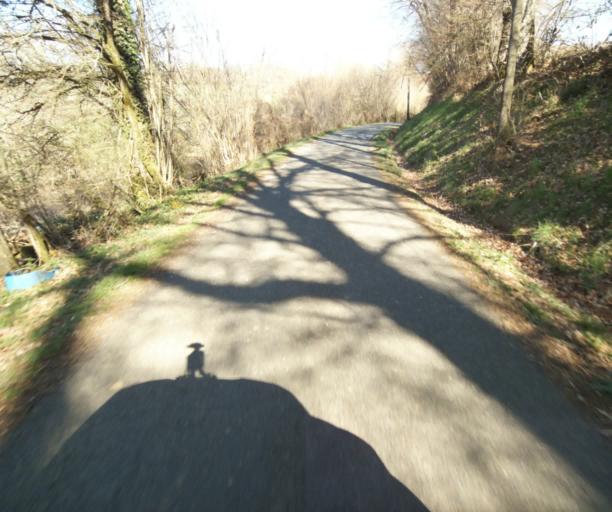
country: FR
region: Limousin
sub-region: Departement de la Correze
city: Chamboulive
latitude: 45.4116
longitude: 1.7234
